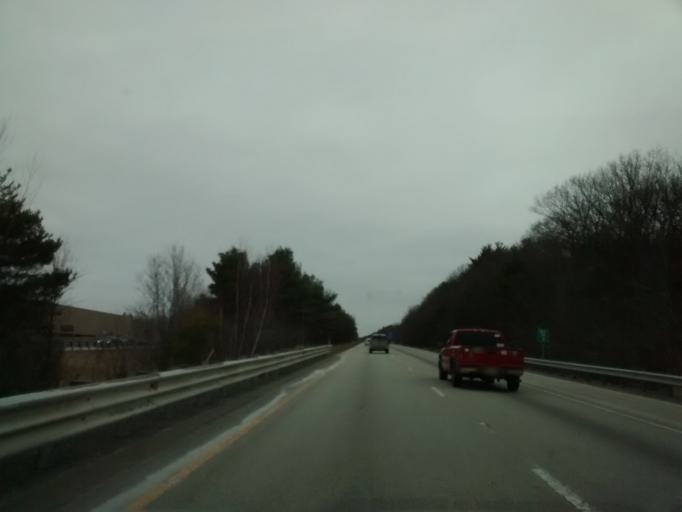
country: US
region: Massachusetts
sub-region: Worcester County
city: Westminster
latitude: 42.5513
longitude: -71.9131
